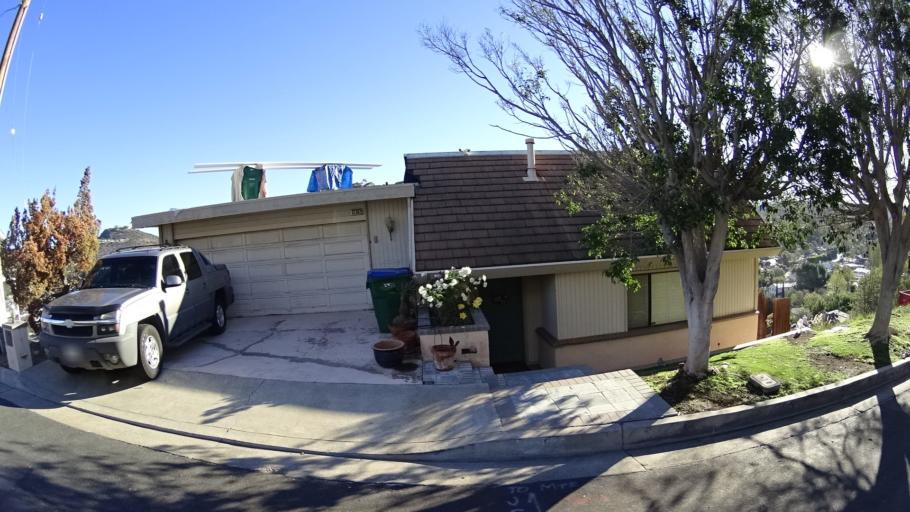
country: US
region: California
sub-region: Orange County
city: North Tustin
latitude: 33.7836
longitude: -117.7979
